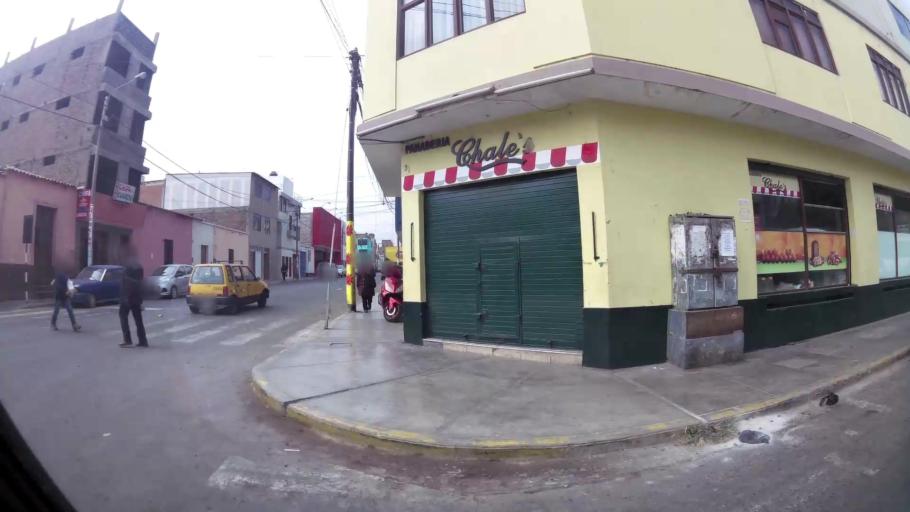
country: PE
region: La Libertad
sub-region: Provincia de Trujillo
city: Trujillo
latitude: -8.1159
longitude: -79.0236
